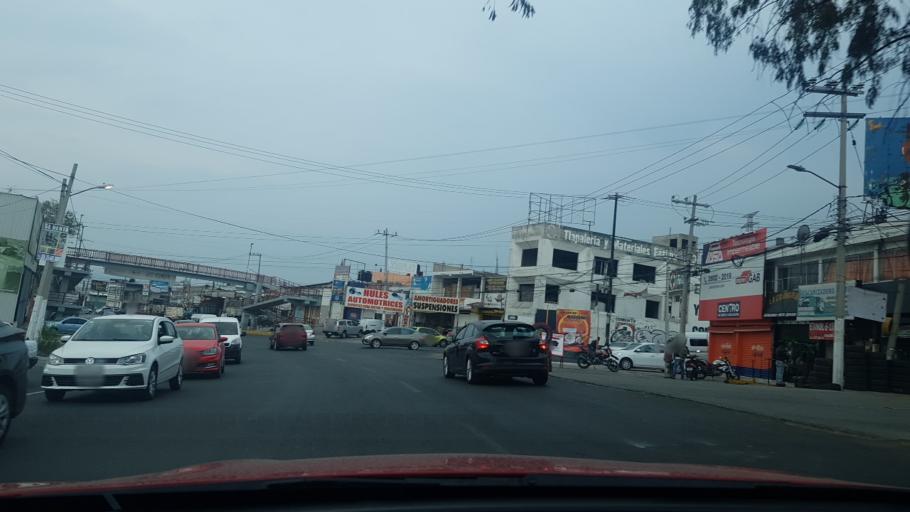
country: MX
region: Mexico
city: Ciudad Lopez Mateos
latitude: 19.6098
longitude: -99.2405
